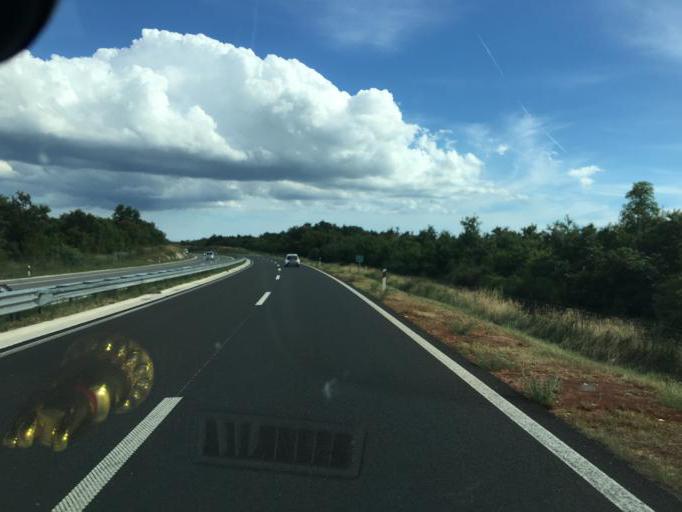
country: HR
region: Istarska
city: Vodnjan
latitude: 45.0362
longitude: 13.8305
